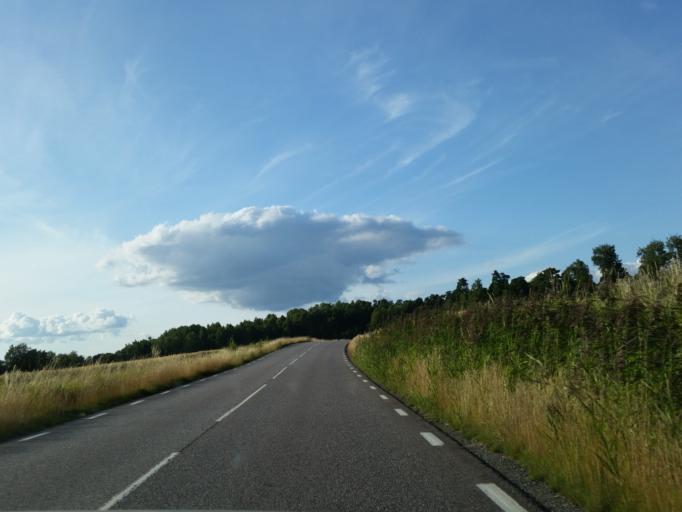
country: SE
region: Soedermanland
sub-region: Gnesta Kommun
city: Gnesta
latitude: 59.0253
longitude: 17.3595
